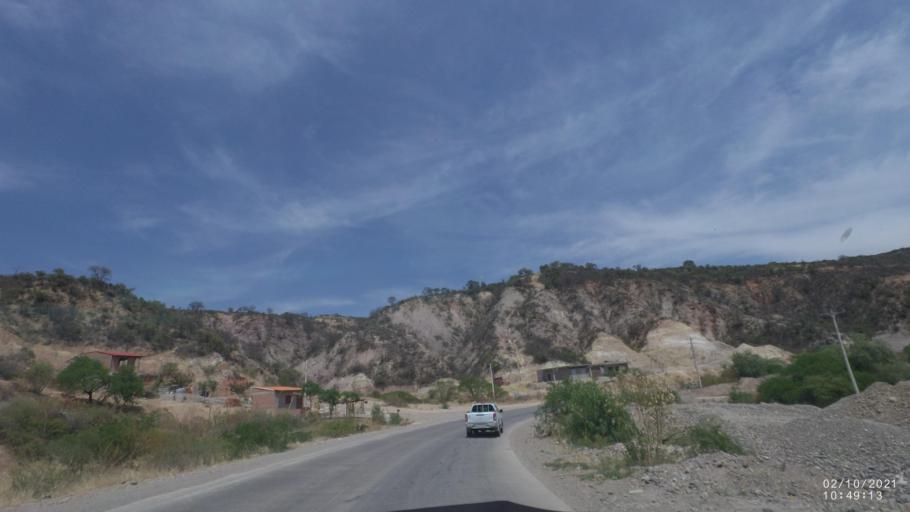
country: BO
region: Cochabamba
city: Sipe Sipe
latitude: -17.5812
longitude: -66.3428
